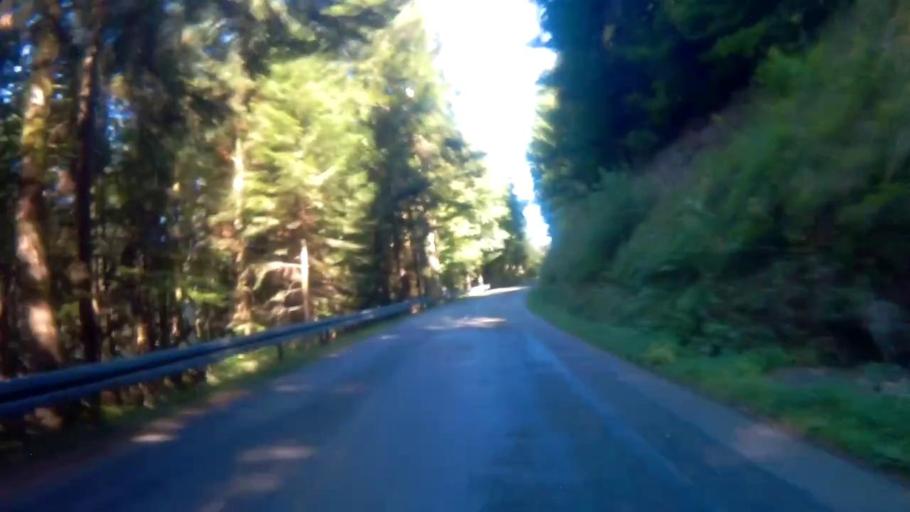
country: DE
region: Baden-Wuerttemberg
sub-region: Freiburg Region
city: Bollen
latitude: 47.7531
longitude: 7.7618
